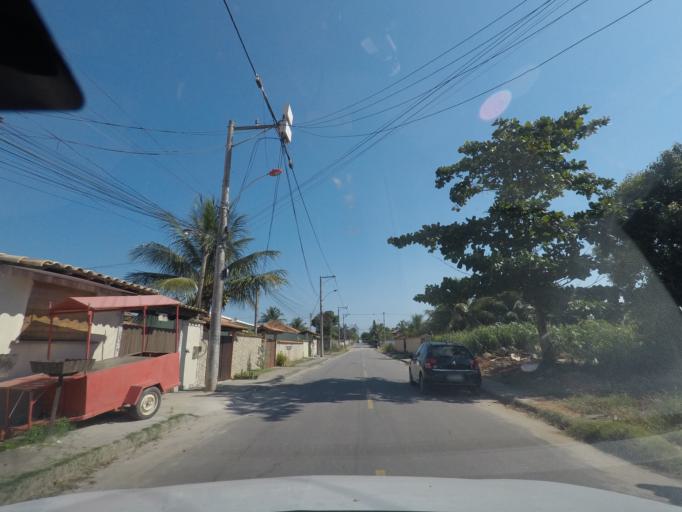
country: BR
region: Rio de Janeiro
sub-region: Niteroi
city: Niteroi
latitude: -22.9612
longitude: -42.9738
